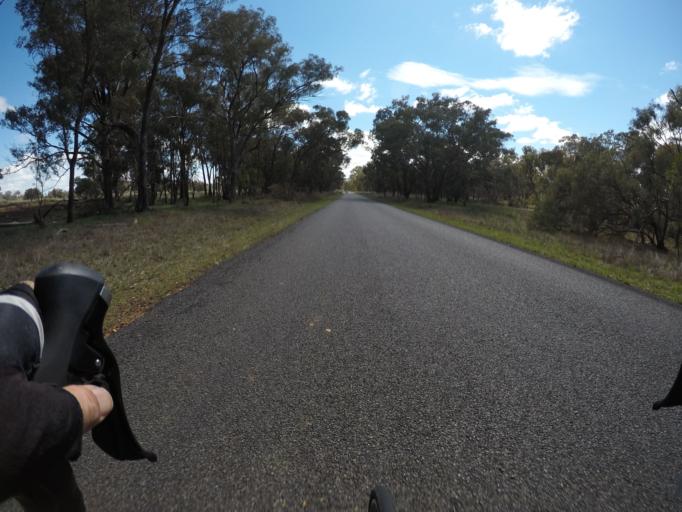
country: AU
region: New South Wales
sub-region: Dubbo Municipality
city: Dubbo
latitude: -32.5361
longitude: 148.5484
